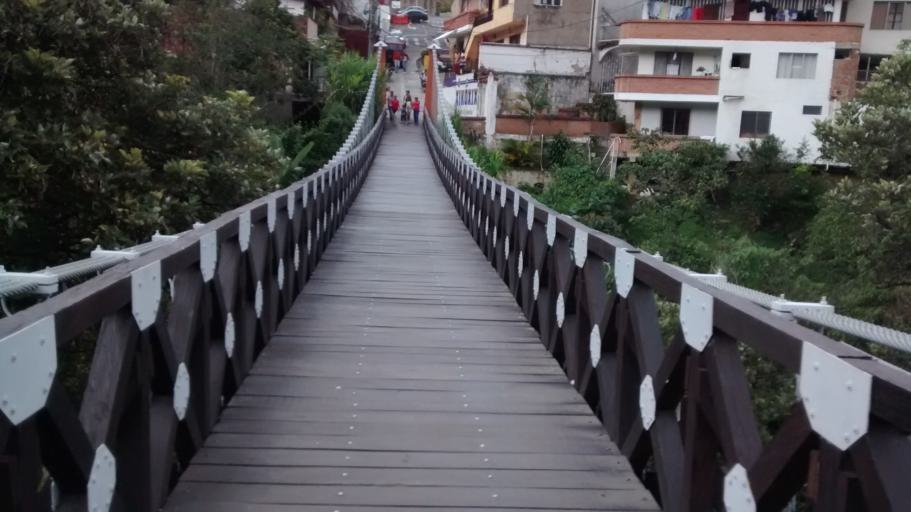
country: CO
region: Antioquia
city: Medellin
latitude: 6.2766
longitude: -75.6359
